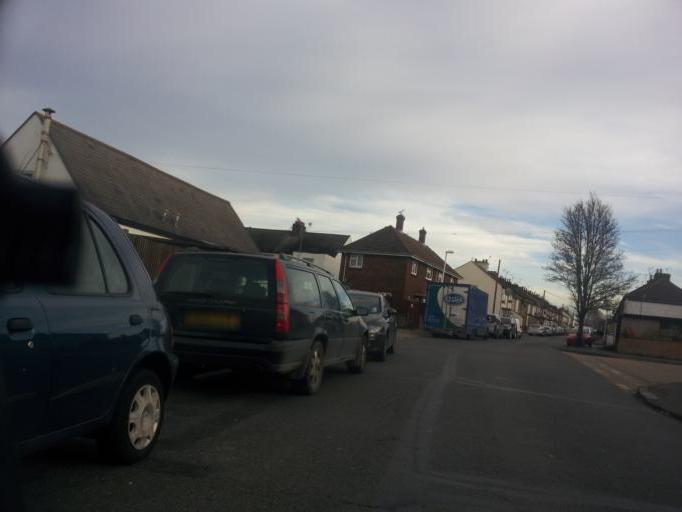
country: GB
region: England
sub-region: Kent
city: Gravesend
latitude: 51.4321
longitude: 0.3529
